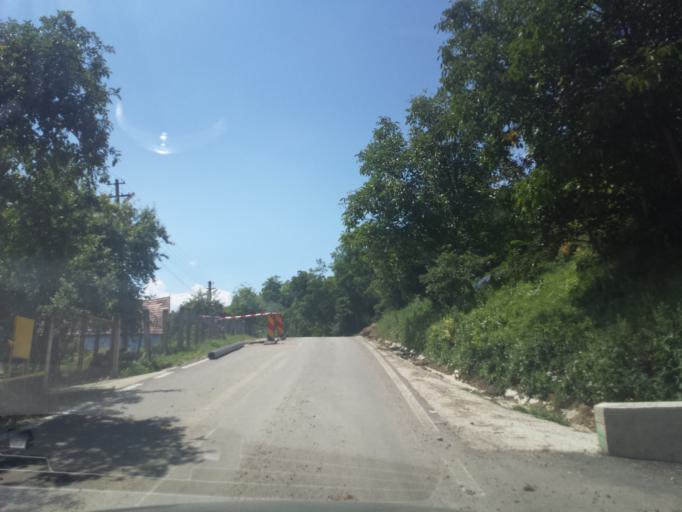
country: RO
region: Cluj
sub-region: Comuna Apahida
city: Dezmir
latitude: 46.7656
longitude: 23.7210
